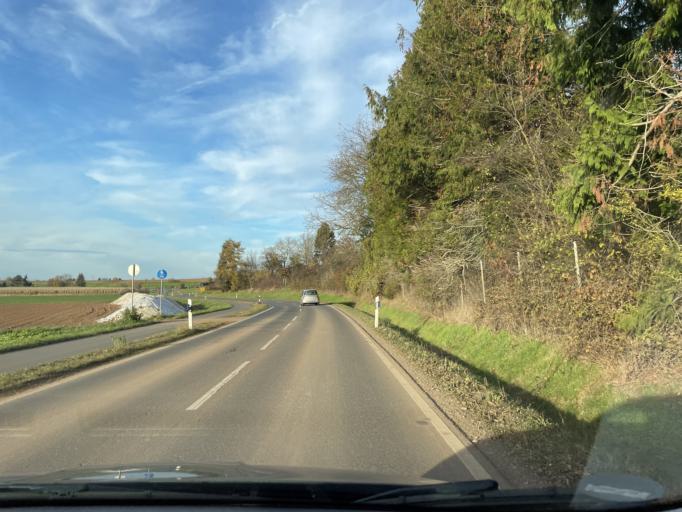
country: DE
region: Hesse
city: Gross-Umstadt
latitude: 49.8776
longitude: 8.9314
